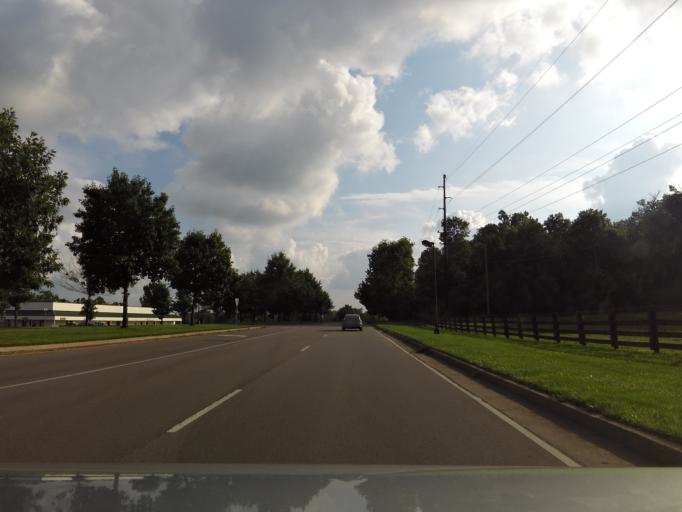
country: US
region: Kentucky
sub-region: Bourbon County
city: Paris
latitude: 38.1867
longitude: -84.2881
